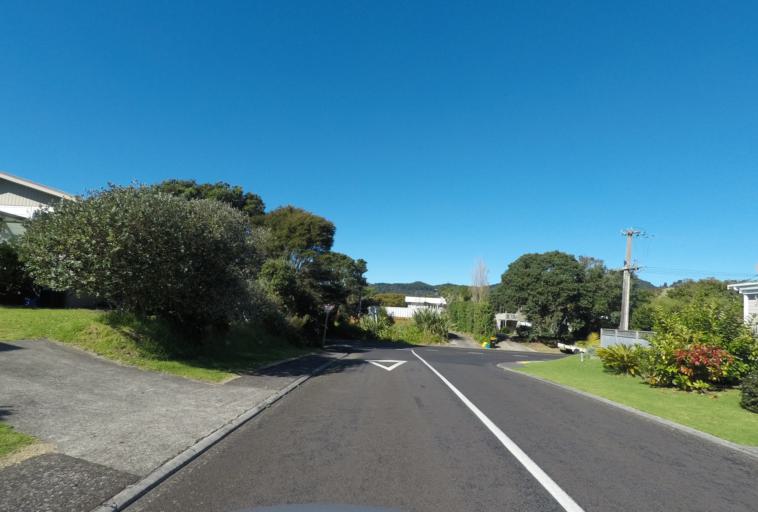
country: NZ
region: Waikato
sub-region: Thames-Coromandel District
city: Whangamata
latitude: -37.2825
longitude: 175.9007
